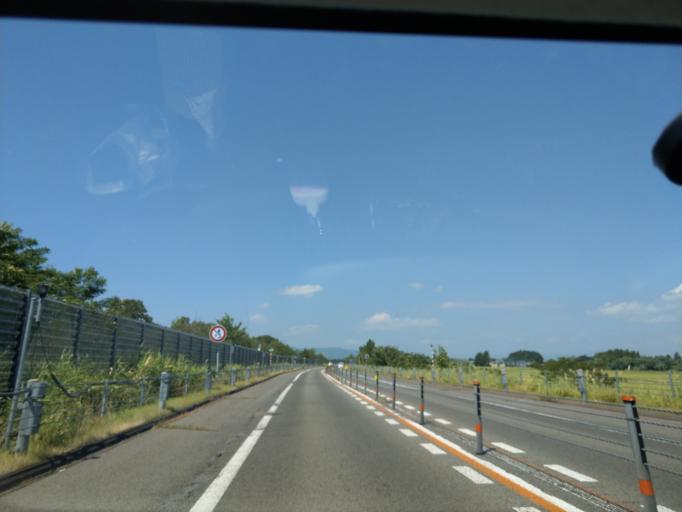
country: JP
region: Akita
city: Yokotemachi
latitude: 39.3454
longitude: 140.4992
